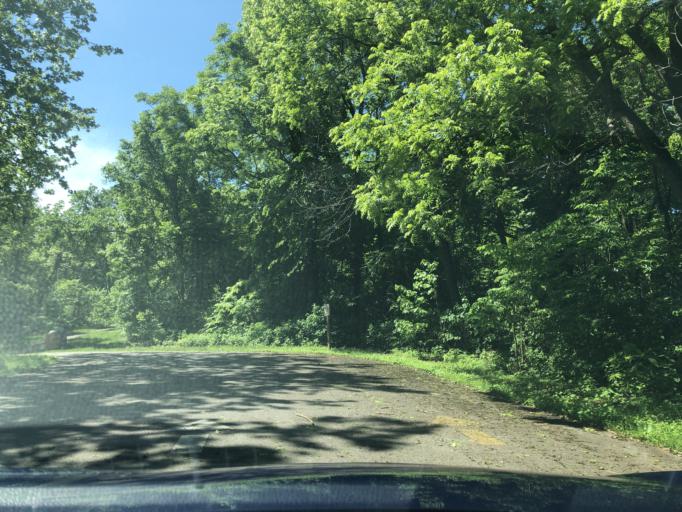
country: US
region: Missouri
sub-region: Platte County
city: Weston
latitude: 39.3883
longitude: -94.8795
